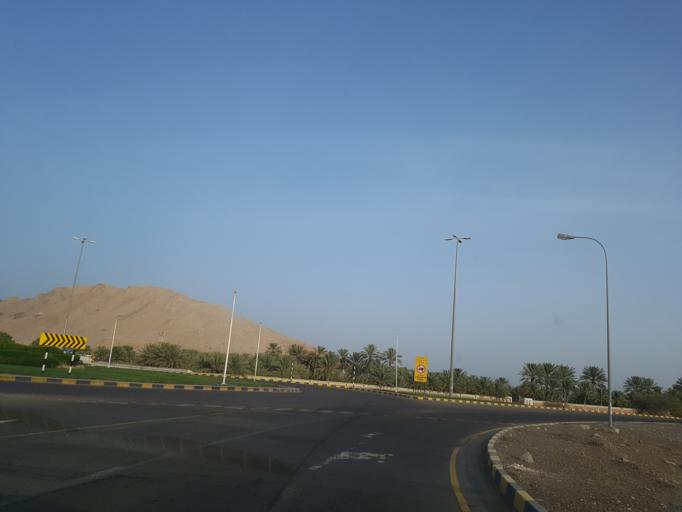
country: OM
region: Al Buraimi
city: Al Buraymi
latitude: 24.2304
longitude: 55.9570
